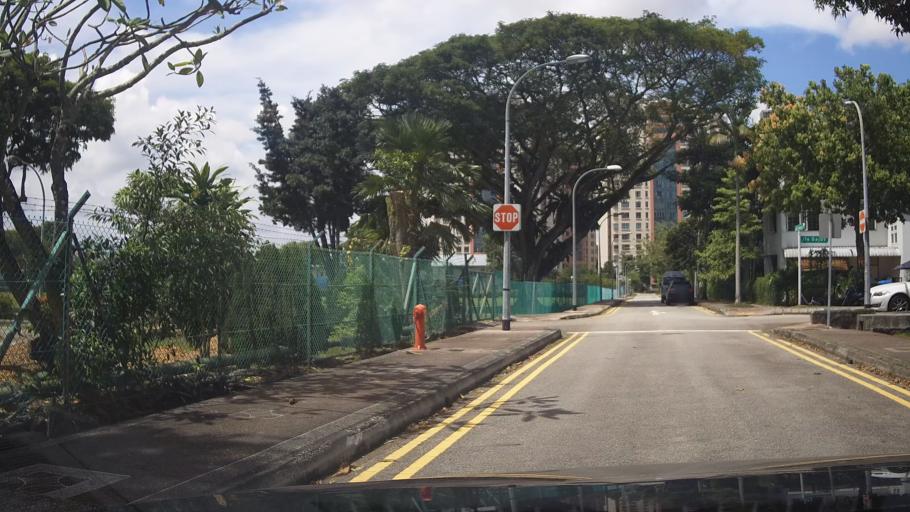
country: SG
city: Singapore
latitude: 1.3037
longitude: 103.8994
